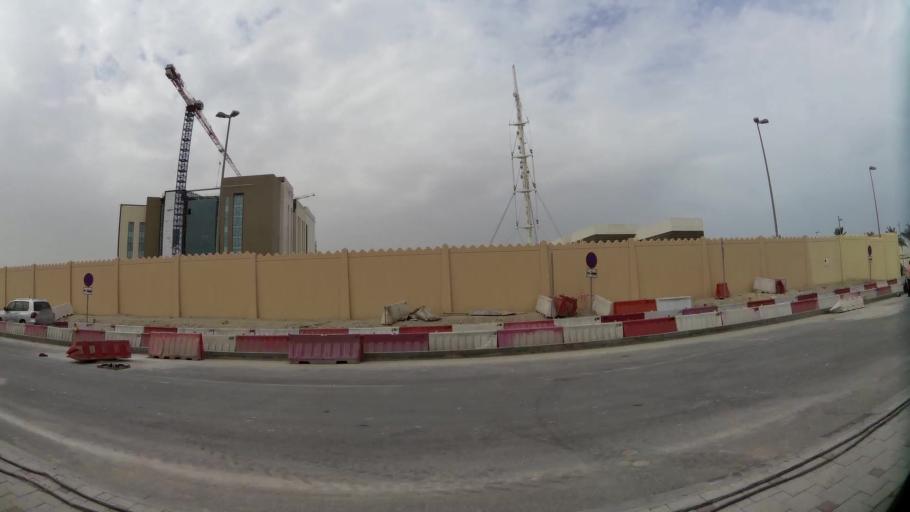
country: QA
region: Baladiyat ar Rayyan
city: Ar Rayyan
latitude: 25.3522
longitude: 51.4570
